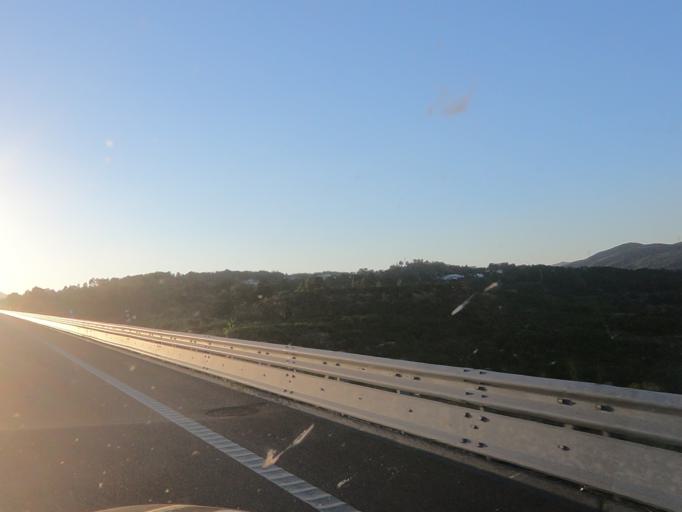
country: PT
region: Vila Real
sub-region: Santa Marta de Penaguiao
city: Santa Marta de Penaguiao
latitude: 41.2650
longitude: -7.7975
